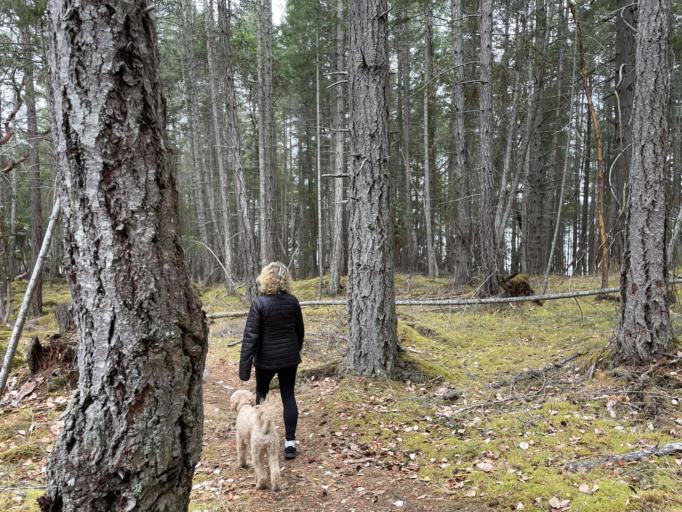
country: CA
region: British Columbia
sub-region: Cowichan Valley Regional District
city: Ladysmith
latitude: 49.0971
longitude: -123.7276
